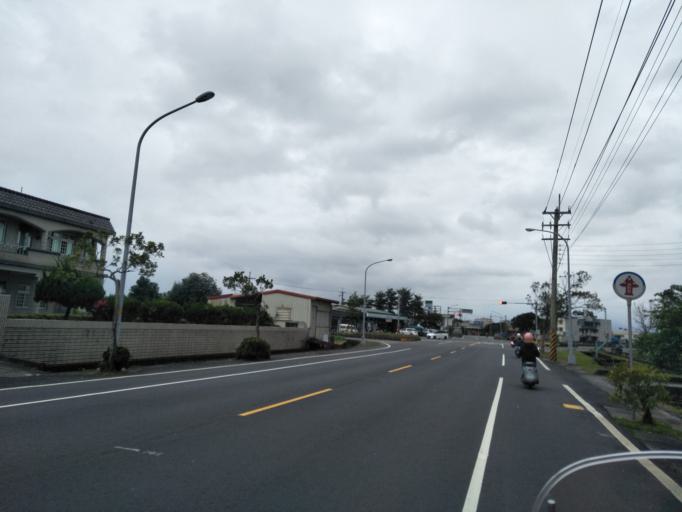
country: TW
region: Taiwan
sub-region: Yilan
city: Yilan
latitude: 24.7762
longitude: 121.7830
